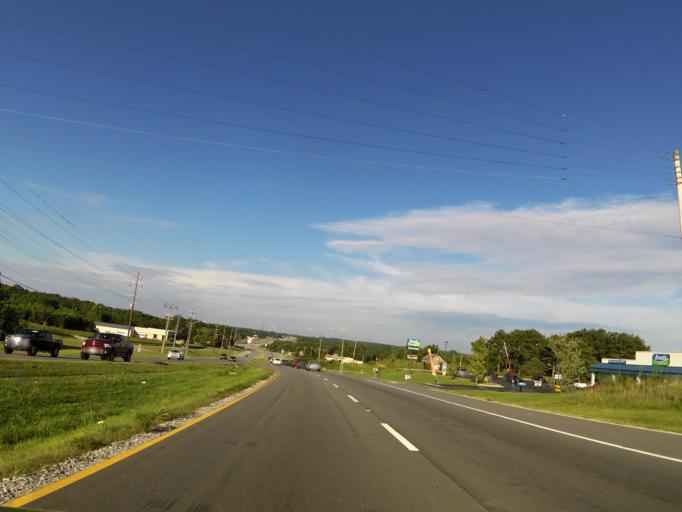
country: US
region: Alabama
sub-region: Lauderdale County
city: Killen
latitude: 34.8451
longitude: -87.5817
